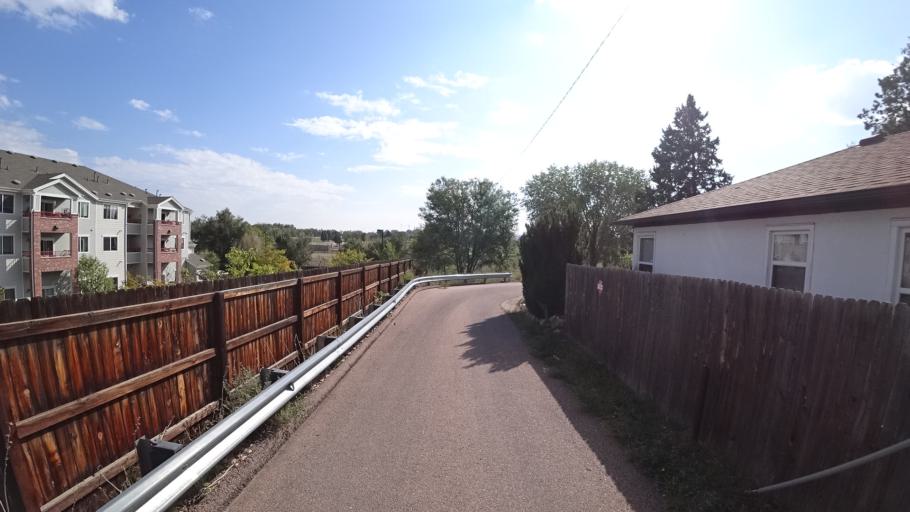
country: US
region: Colorado
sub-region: El Paso County
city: Colorado Springs
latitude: 38.8312
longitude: -104.8061
